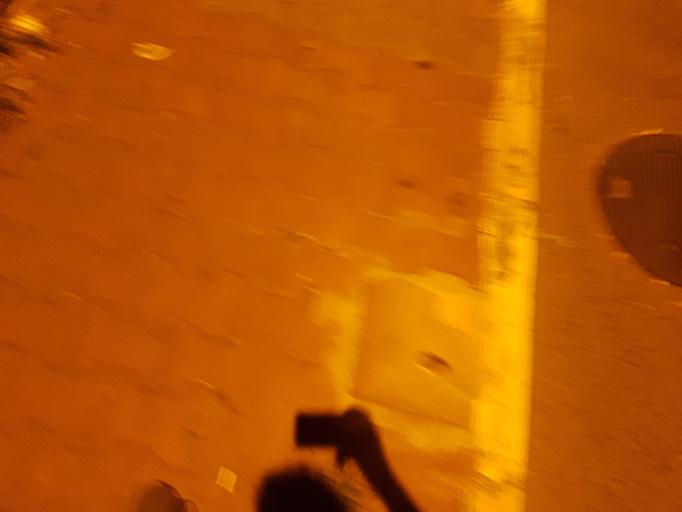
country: TR
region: Istanbul
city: Bahcelievler
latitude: 40.9579
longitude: 28.8220
